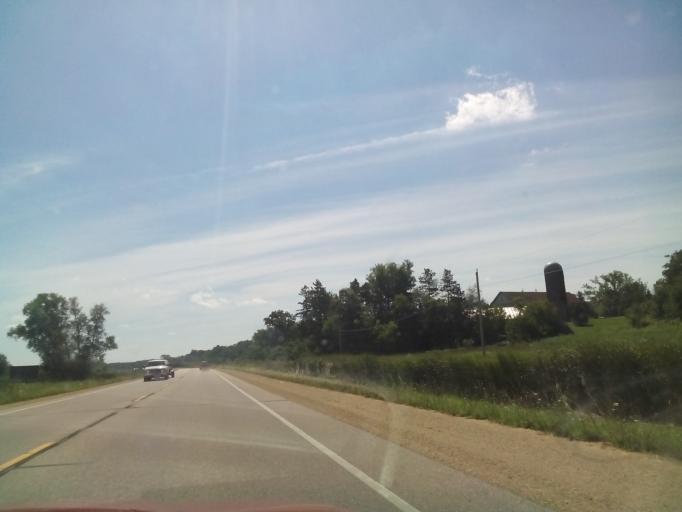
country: US
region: Wisconsin
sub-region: Green County
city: Monticello
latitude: 42.7577
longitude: -89.6125
